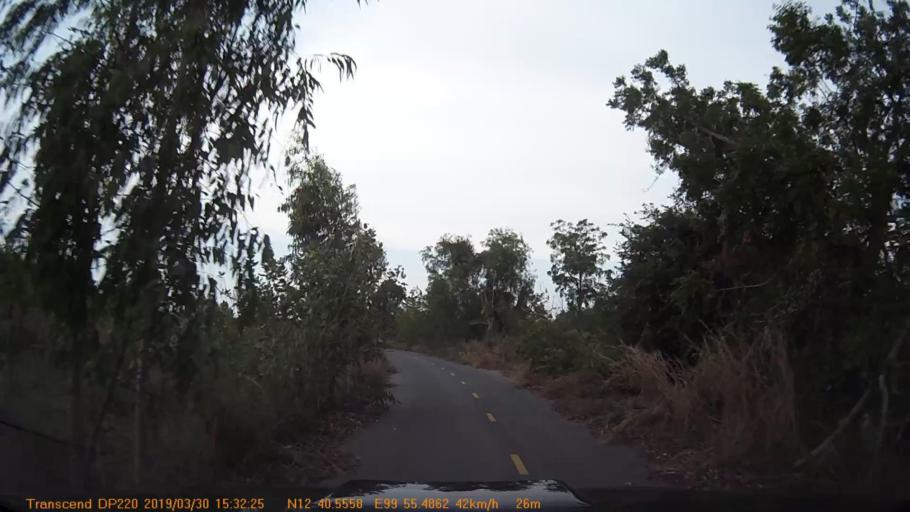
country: TH
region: Prachuap Khiri Khan
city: Hua Hin
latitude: 12.6760
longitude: 99.9250
